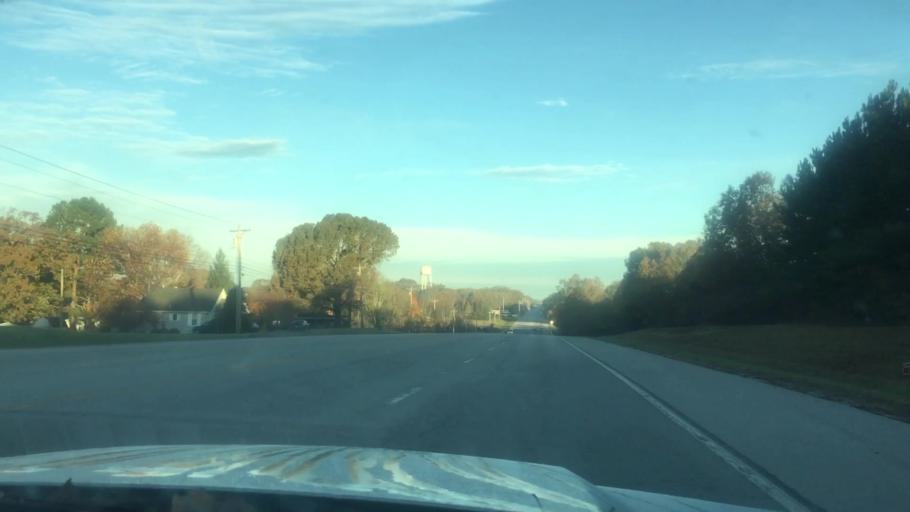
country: US
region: Tennessee
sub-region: Coffee County
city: Tullahoma
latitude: 35.3272
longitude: -86.1782
